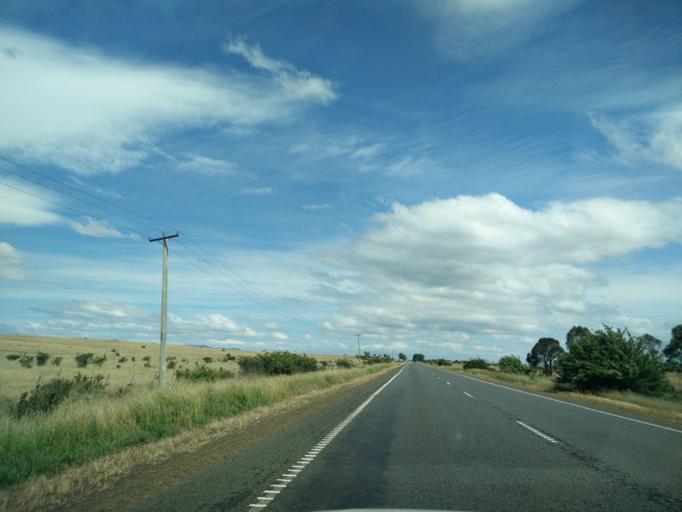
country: AU
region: Tasmania
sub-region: Northern Midlands
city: Evandale
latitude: -41.8553
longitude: 147.4532
